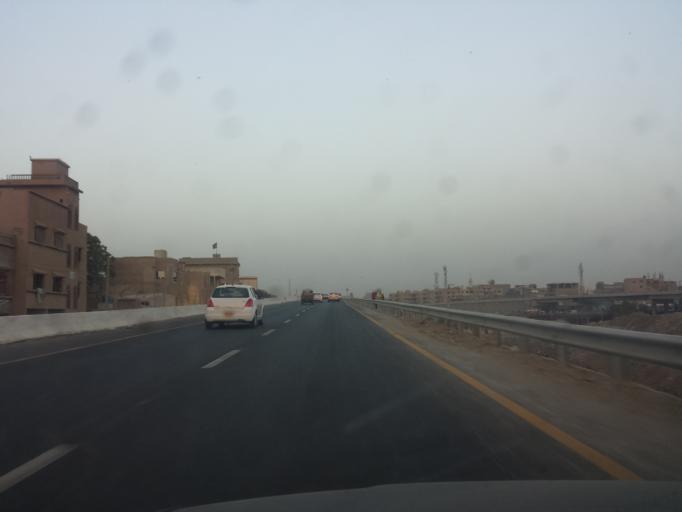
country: PK
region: Sindh
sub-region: Karachi District
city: Karachi
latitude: 24.8939
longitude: 67.0408
